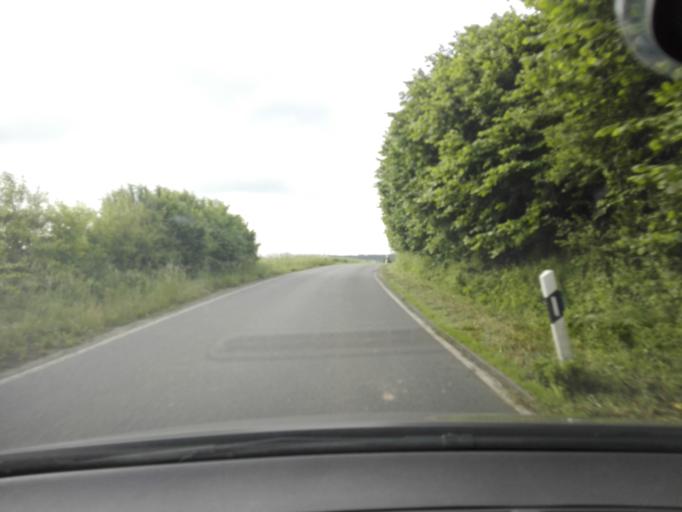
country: DE
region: North Rhine-Westphalia
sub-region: Regierungsbezirk Arnsberg
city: Frondenberg
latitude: 51.5109
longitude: 7.7337
